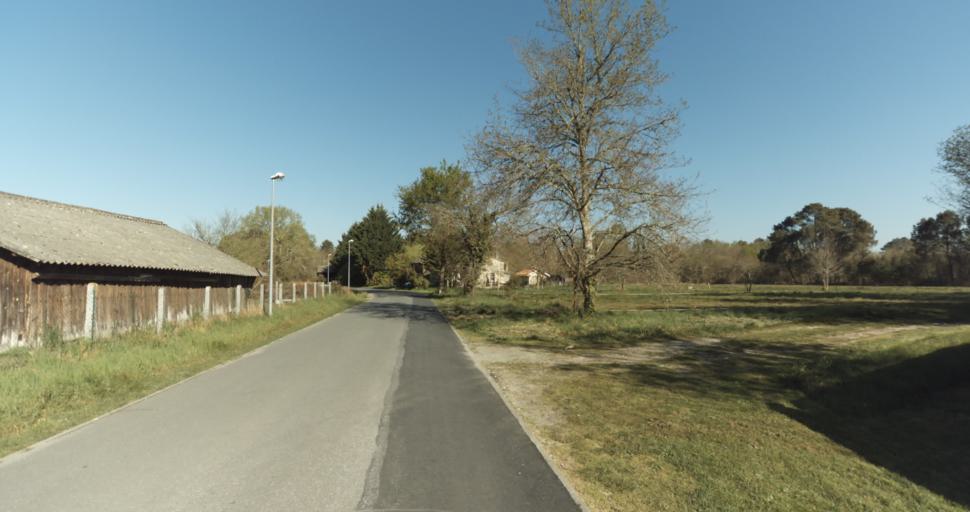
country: FR
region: Aquitaine
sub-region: Departement de la Gironde
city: Martignas-sur-Jalle
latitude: 44.8038
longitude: -0.8410
